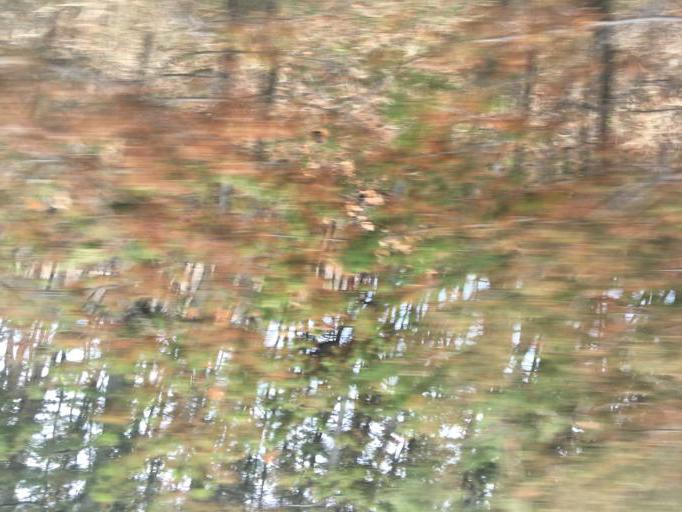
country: JP
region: Aomori
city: Shimokizukuri
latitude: 40.6830
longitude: 139.9662
